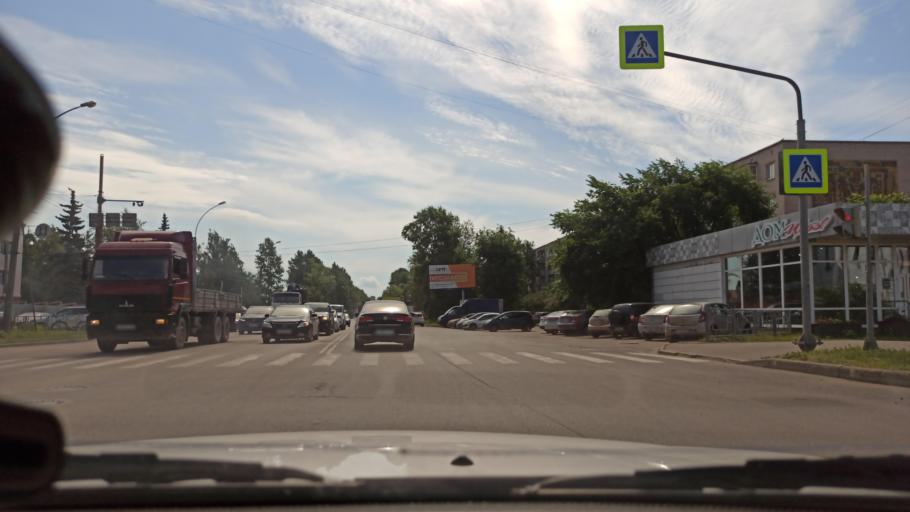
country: RU
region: Vologda
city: Vologda
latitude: 59.2120
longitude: 39.8523
